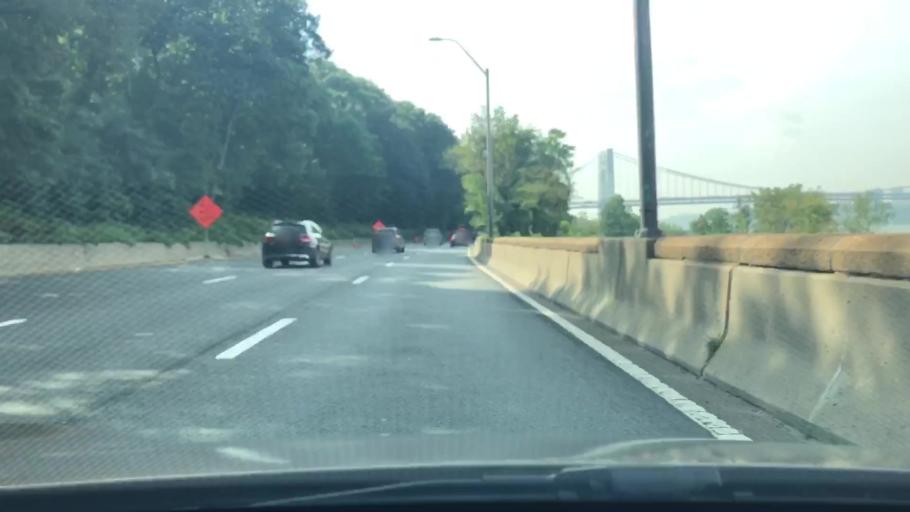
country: US
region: New York
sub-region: New York County
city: Inwood
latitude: 40.8644
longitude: -73.9338
